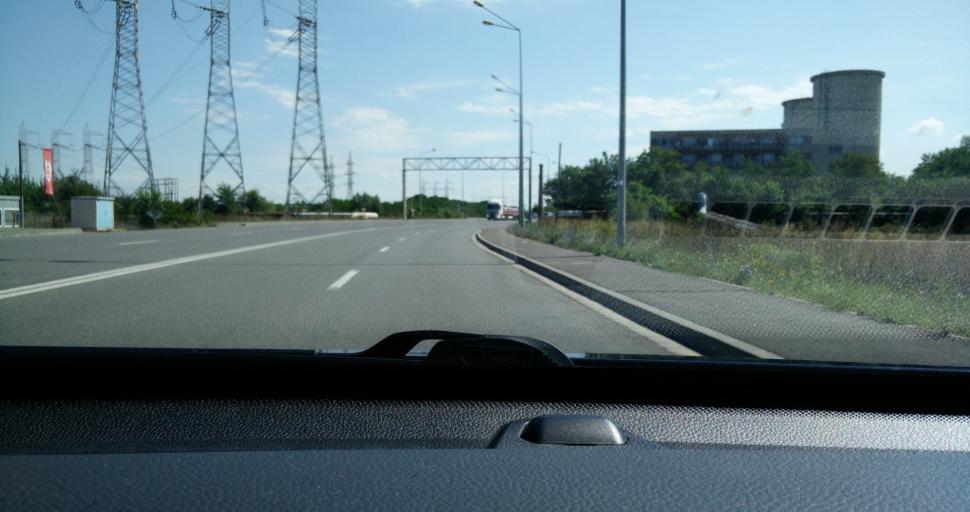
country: RO
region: Bihor
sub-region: Comuna Sanmartin
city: Sanmartin
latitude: 47.0304
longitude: 21.9793
